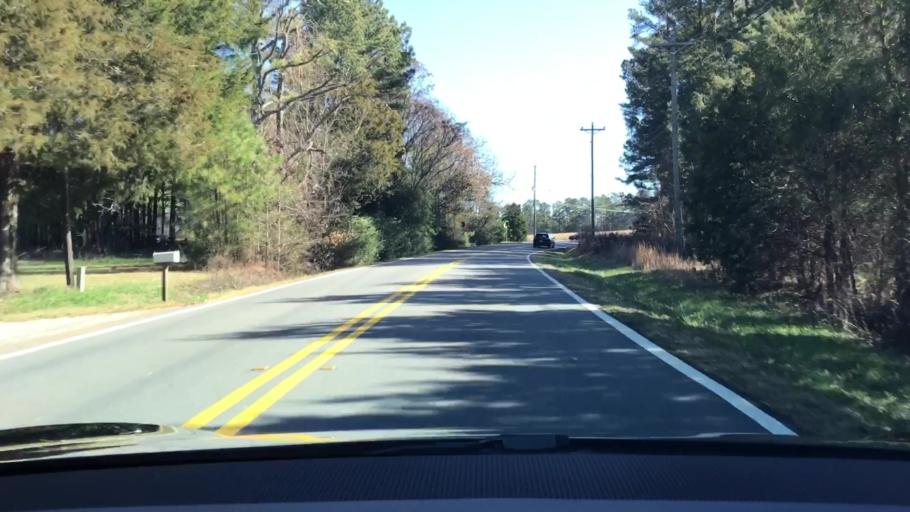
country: US
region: Georgia
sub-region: Barrow County
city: Winder
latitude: 33.8994
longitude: -83.7898
